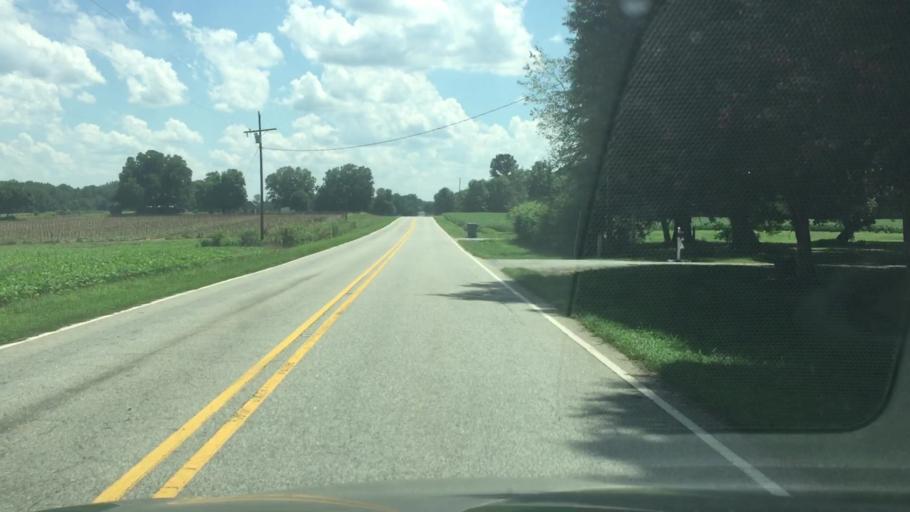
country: US
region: North Carolina
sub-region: Rowan County
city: China Grove
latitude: 35.6396
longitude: -80.6394
